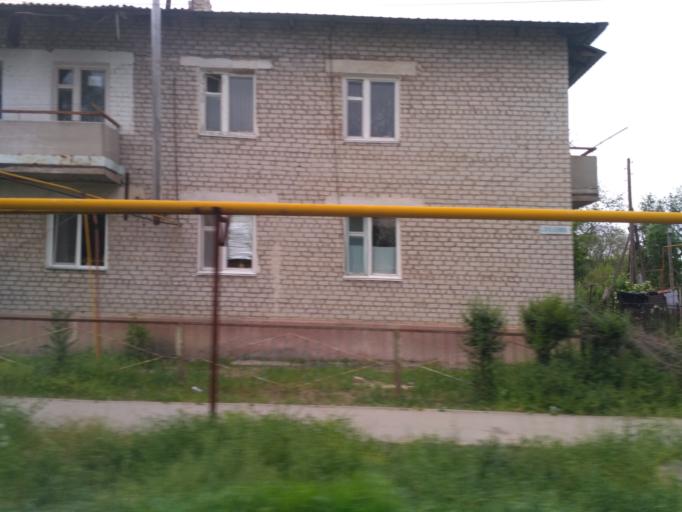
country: KZ
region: Almaty Oblysy
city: Burunday
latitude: 43.4571
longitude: 76.7245
